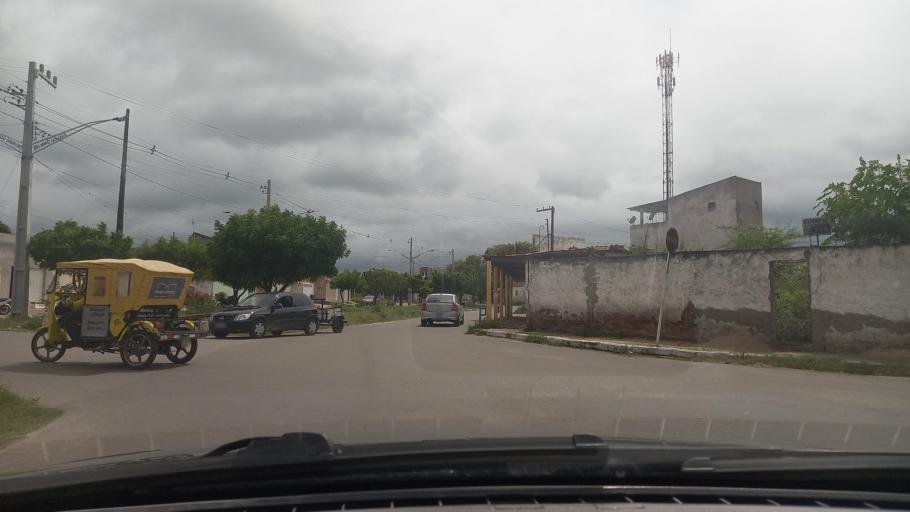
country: BR
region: Alagoas
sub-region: Delmiro Gouveia
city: Delmiro Gouveia
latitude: -9.3832
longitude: -38.0034
